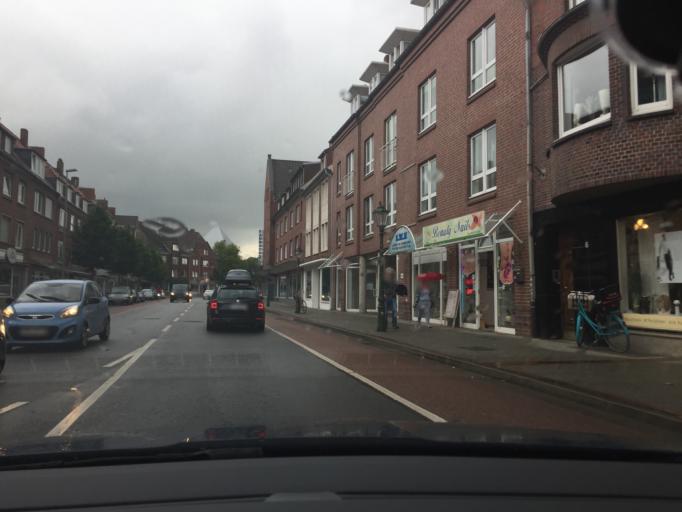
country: DE
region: Lower Saxony
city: Emden
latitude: 53.3659
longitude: 7.2070
